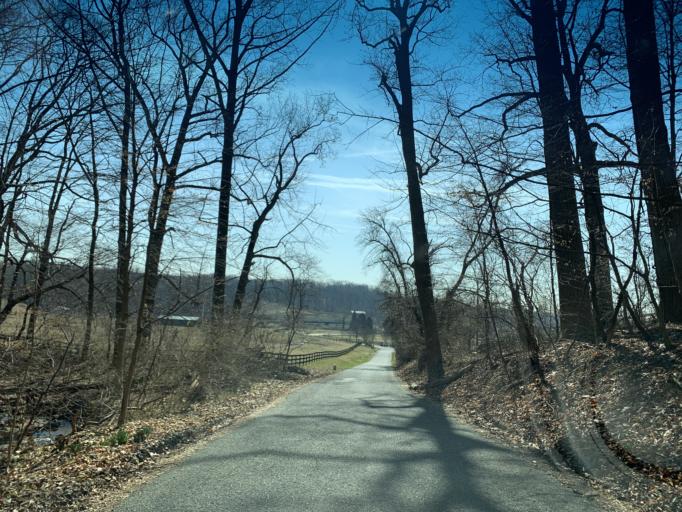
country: US
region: Maryland
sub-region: Baltimore County
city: Kingsville
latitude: 39.4786
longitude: -76.4662
